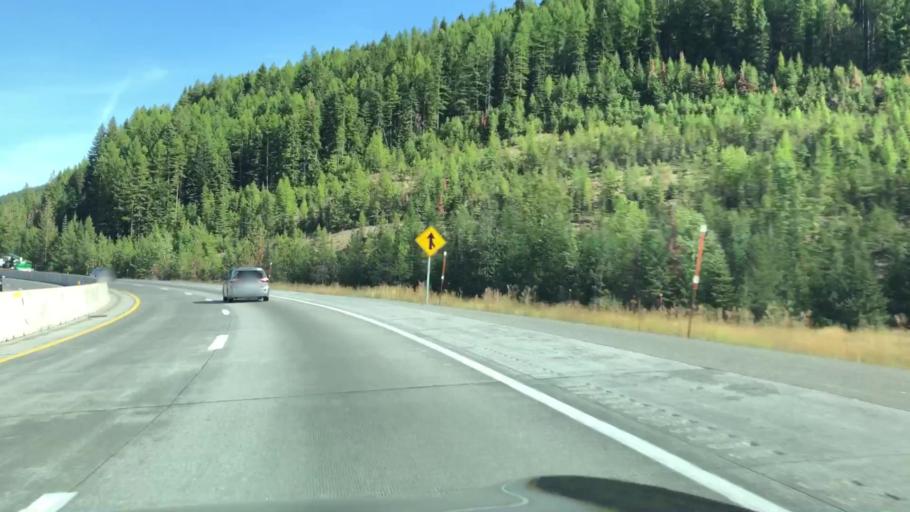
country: US
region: Idaho
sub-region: Shoshone County
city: Wallace
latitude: 47.4610
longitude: -115.7358
